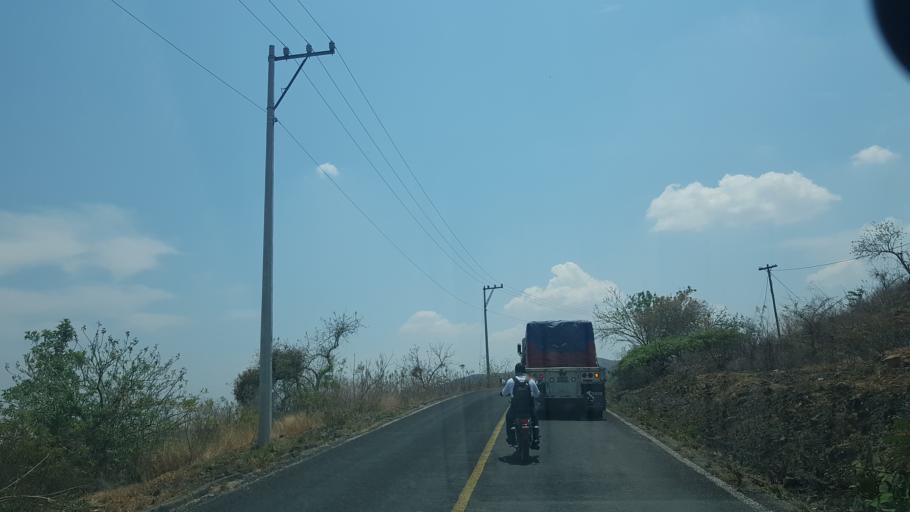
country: MX
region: Puebla
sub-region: Atzitzihuacan
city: Santiago Atzitzihuacan
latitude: 18.8330
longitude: -98.5879
